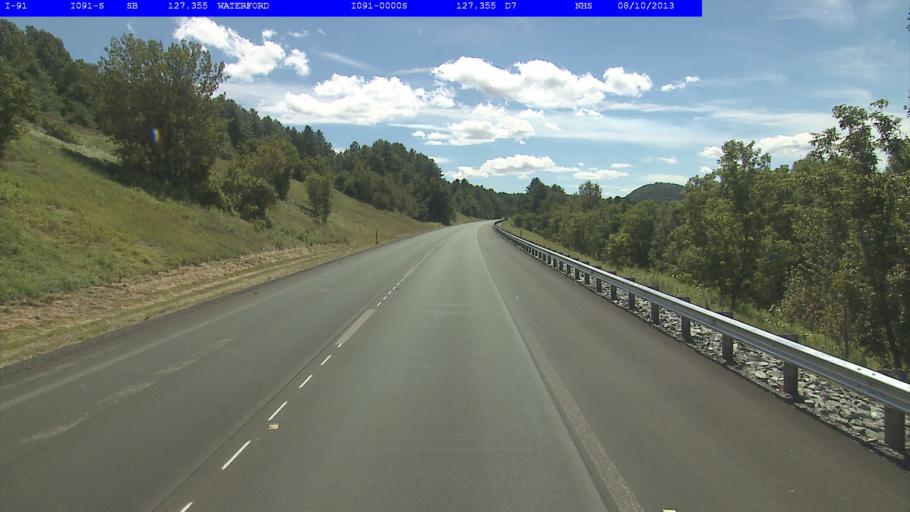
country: US
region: Vermont
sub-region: Caledonia County
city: Saint Johnsbury
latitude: 44.3836
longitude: -72.0188
